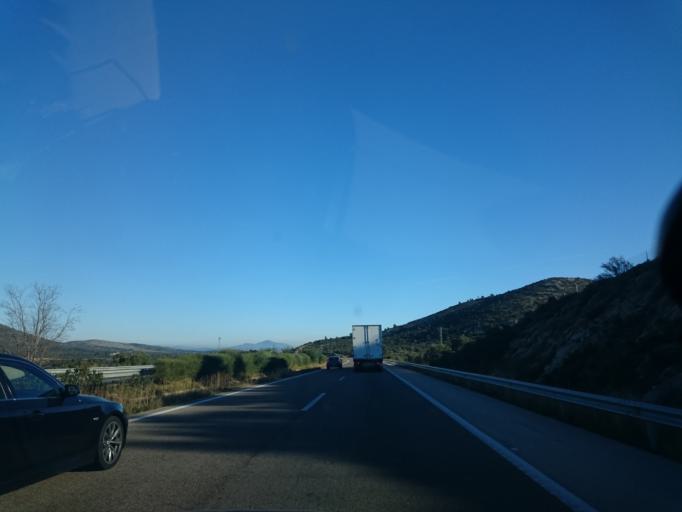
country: ES
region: Valencia
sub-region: Provincia de Castello
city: Santa Magdalena de Pulpis
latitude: 40.3762
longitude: 0.3372
